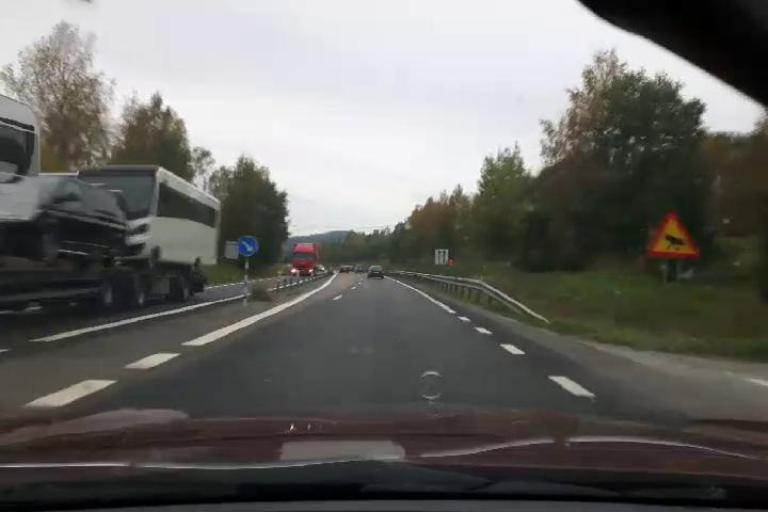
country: SE
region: Vaesternorrland
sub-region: OErnskoeldsviks Kommun
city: Ornskoldsvik
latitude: 63.2979
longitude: 18.6505
